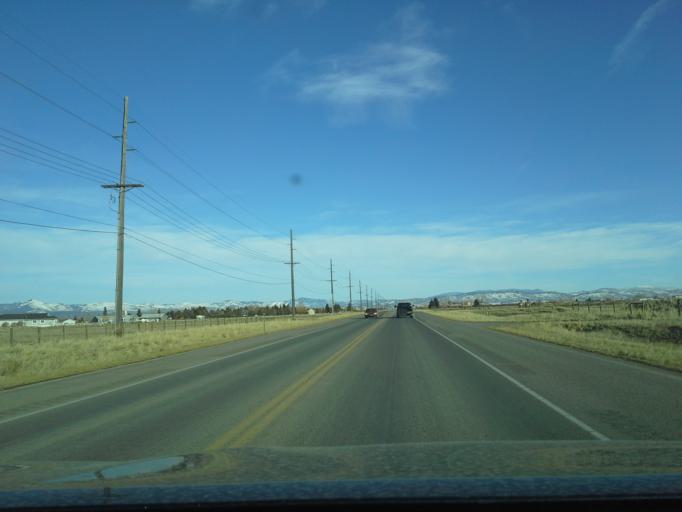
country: US
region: Montana
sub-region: Lewis and Clark County
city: Helena Valley Southeast
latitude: 46.6168
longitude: -111.9562
